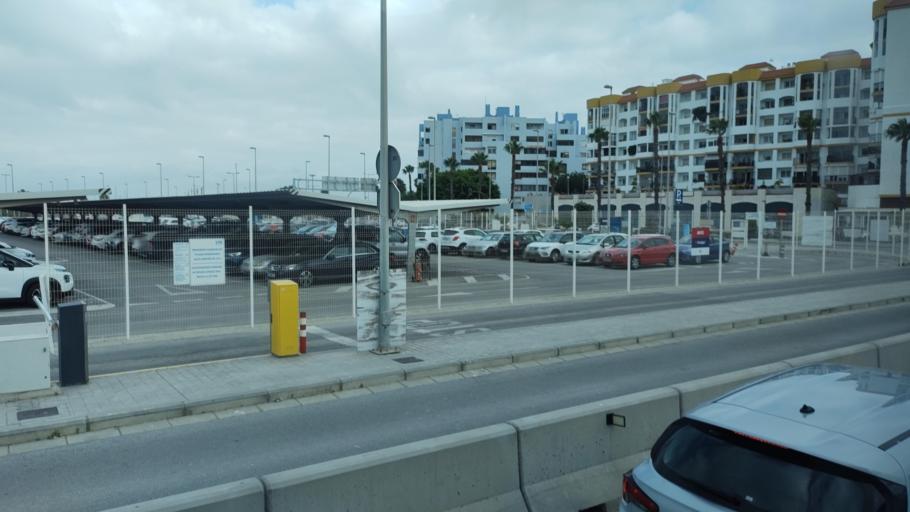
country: GI
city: Gibraltar
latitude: 36.1555
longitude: -5.3495
